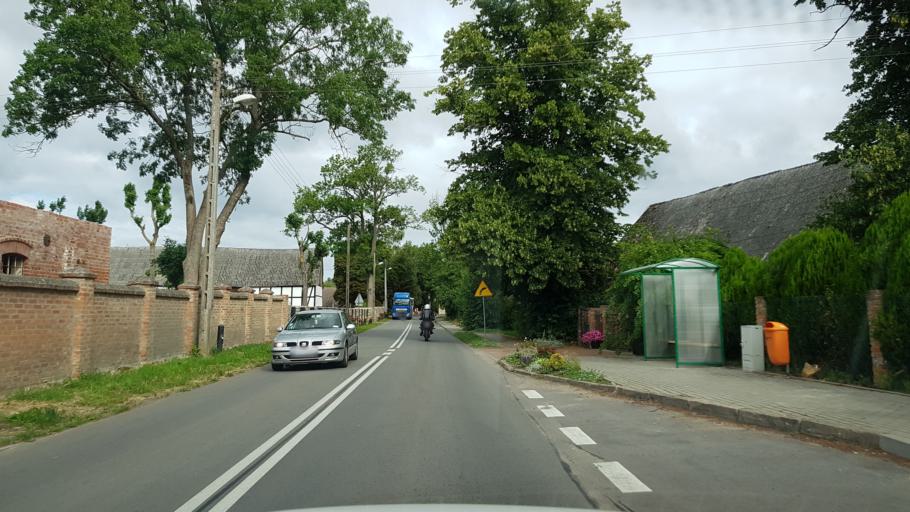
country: PL
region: West Pomeranian Voivodeship
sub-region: Powiat gryficki
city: Rewal
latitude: 54.0582
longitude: 15.0249
